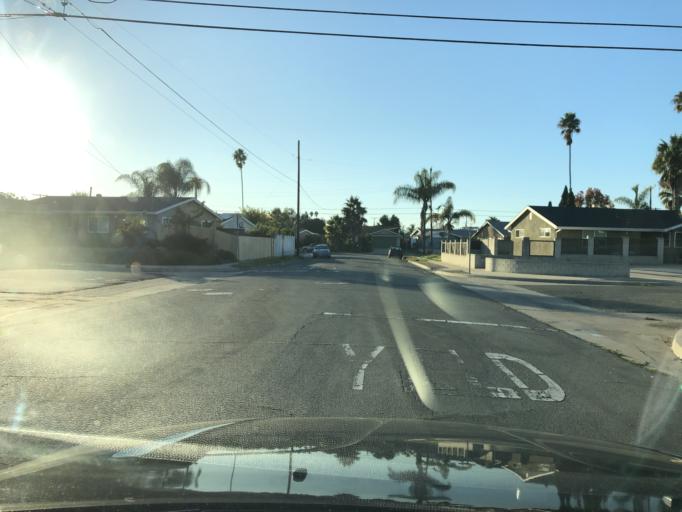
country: US
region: California
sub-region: San Diego County
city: La Jolla
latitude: 32.8187
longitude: -117.1936
